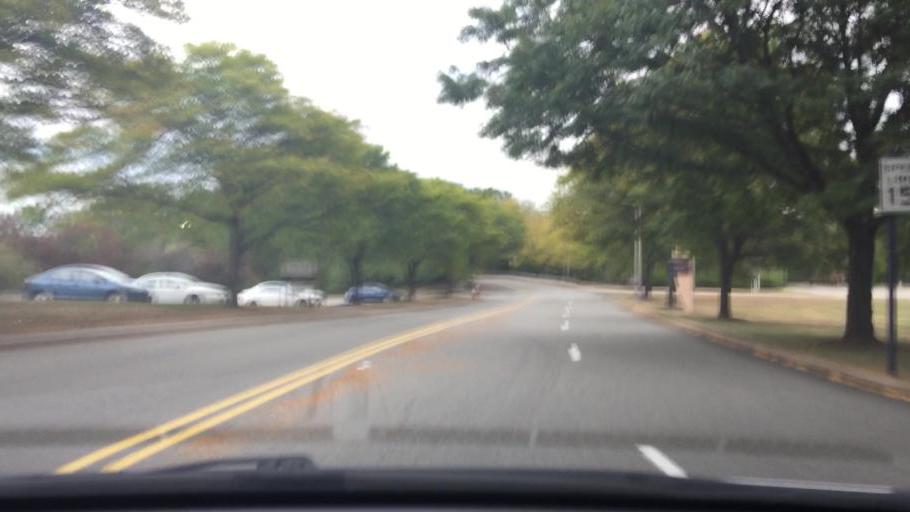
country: US
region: New Jersey
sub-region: Bergen County
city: Paramus
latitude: 40.9536
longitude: -74.0720
